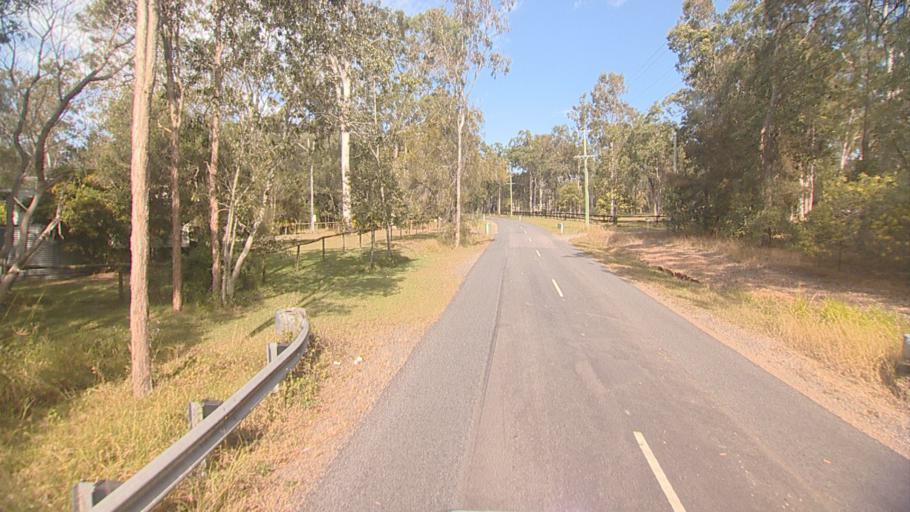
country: AU
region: Queensland
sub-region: Logan
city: North Maclean
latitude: -27.7508
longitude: 152.9734
